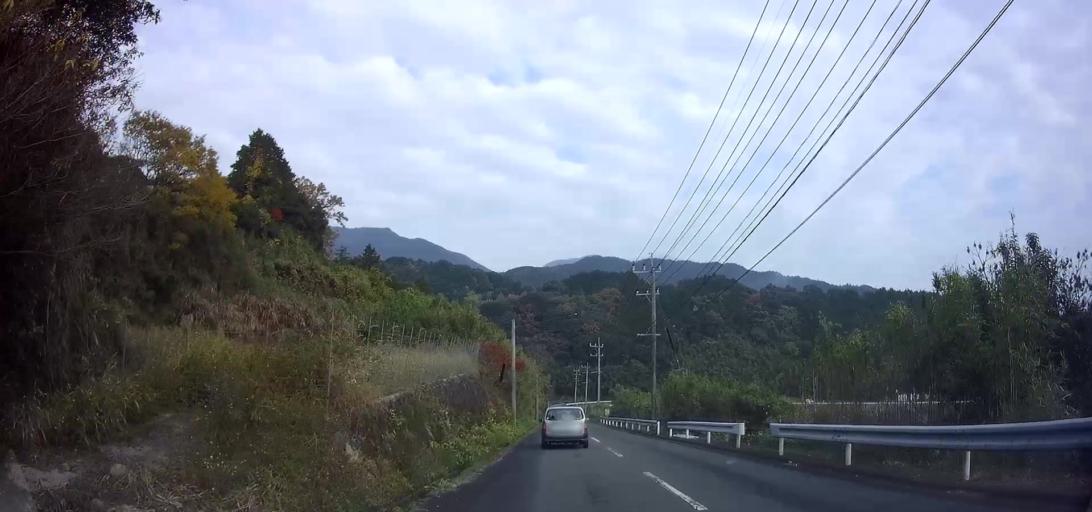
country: JP
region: Nagasaki
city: Shimabara
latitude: 32.6858
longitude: 130.2841
